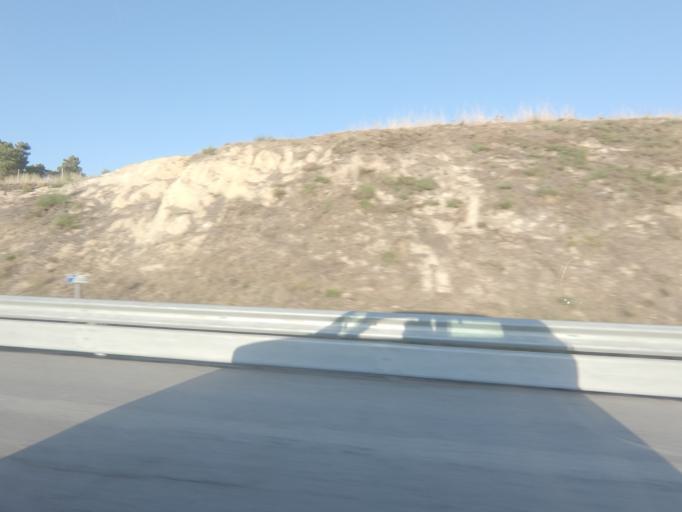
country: PT
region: Vila Real
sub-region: Vila Real
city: Vila Real
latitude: 41.2955
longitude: -7.6938
